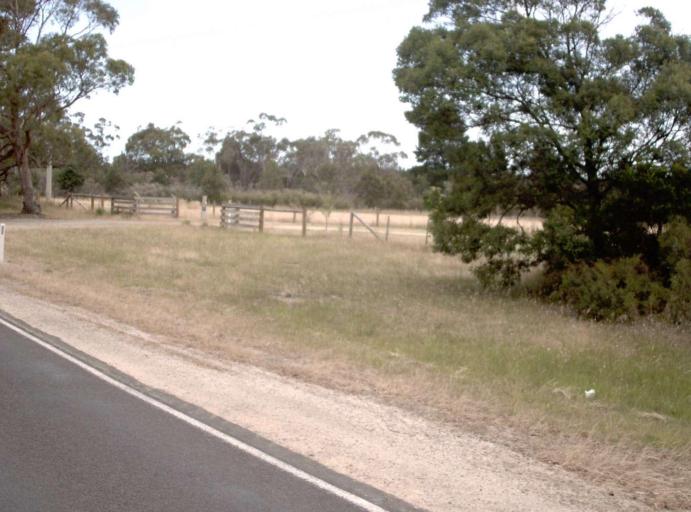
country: AU
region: Victoria
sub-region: Wellington
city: Sale
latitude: -38.2118
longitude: 147.1030
